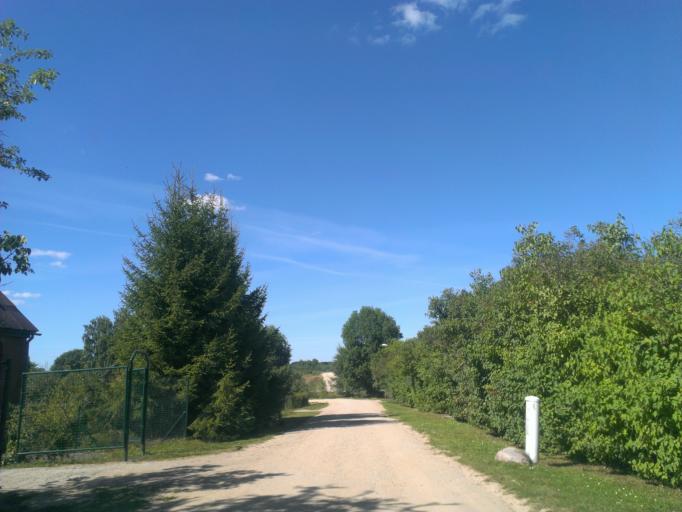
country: LV
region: Malpils
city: Malpils
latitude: 57.0115
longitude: 24.9680
